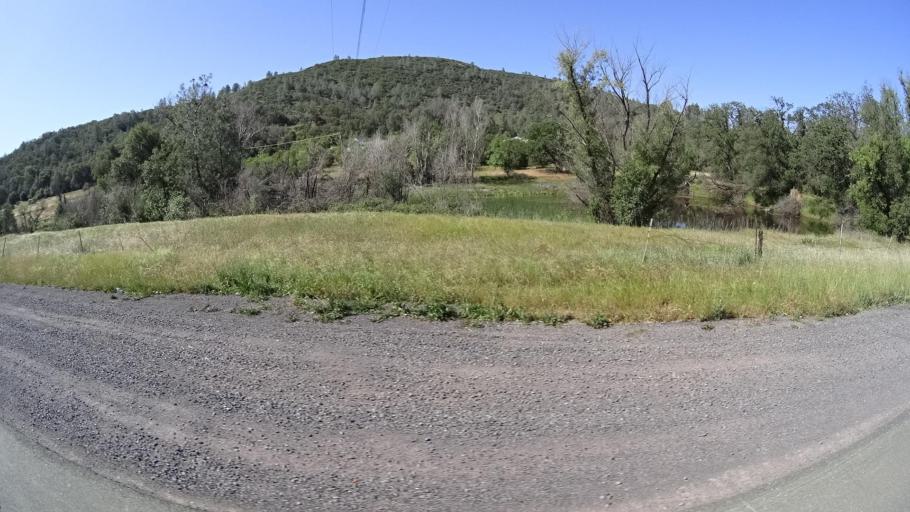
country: US
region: California
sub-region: Lake County
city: Clearlake Oaks
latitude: 39.0123
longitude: -122.6289
